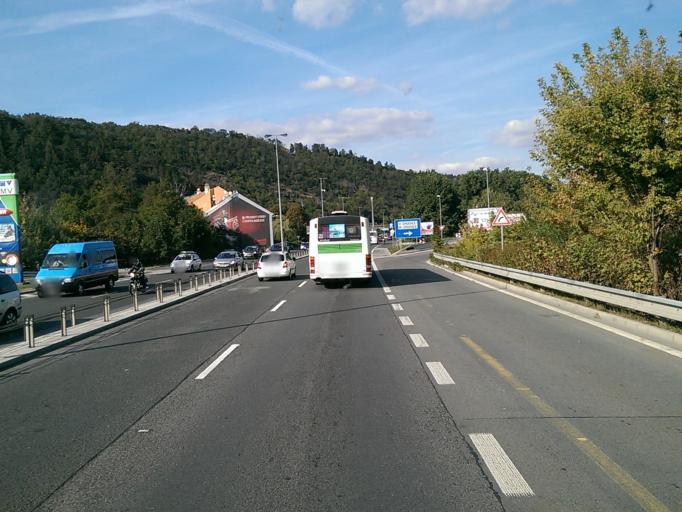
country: CZ
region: Praha
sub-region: Praha 12
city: Modrany
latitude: 50.0222
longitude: 14.3943
